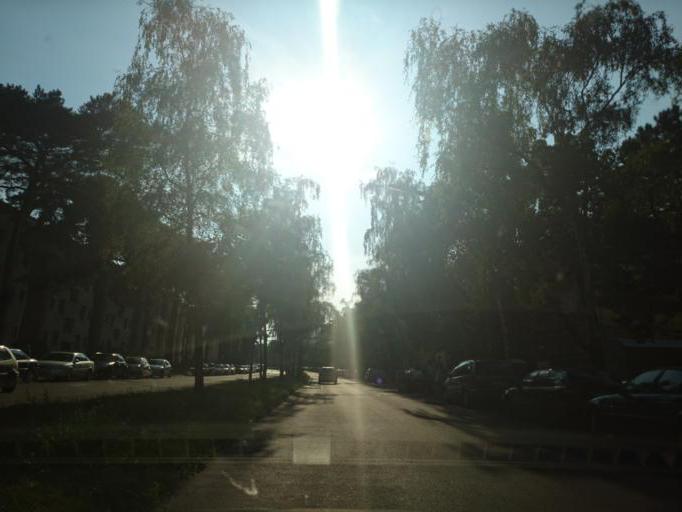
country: DE
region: Berlin
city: Zehlendorf Bezirk
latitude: 52.4516
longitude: 13.2608
